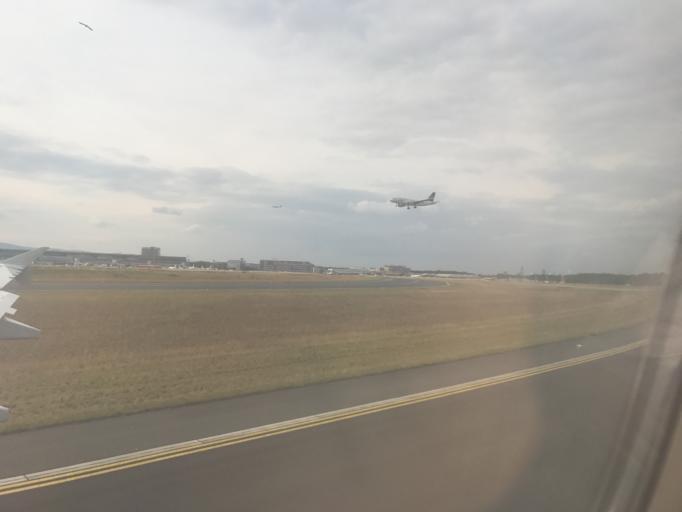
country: DE
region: Hesse
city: Morfelden-Walldorf
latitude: 50.0390
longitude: 8.5935
